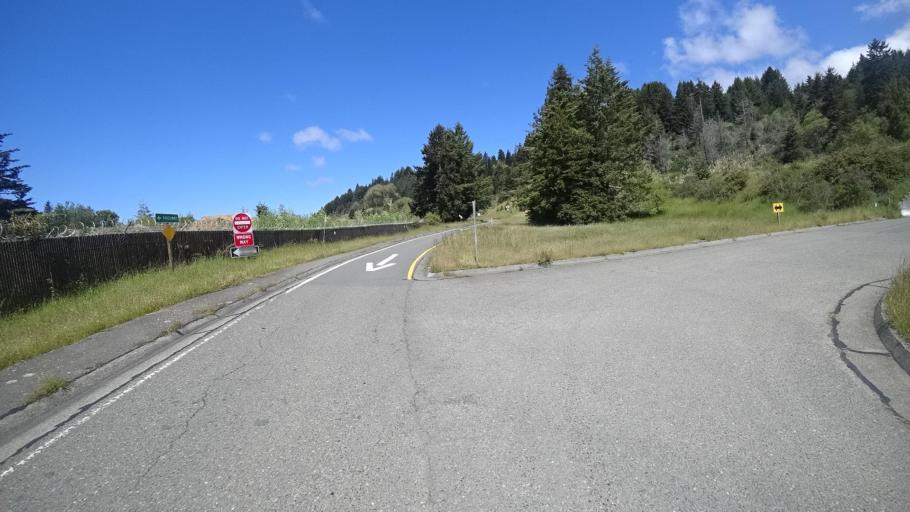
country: US
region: California
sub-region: Humboldt County
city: Arcata
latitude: 40.9076
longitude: -124.0459
